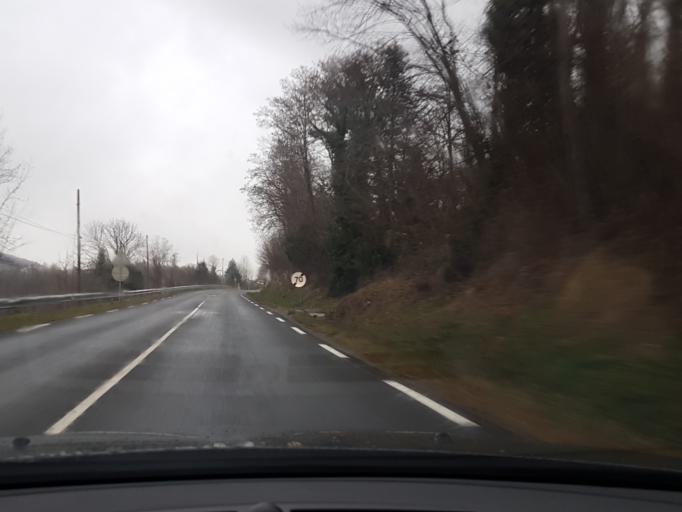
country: FR
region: Midi-Pyrenees
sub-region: Departement de l'Ariege
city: Foix
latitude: 42.9881
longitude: 1.5563
